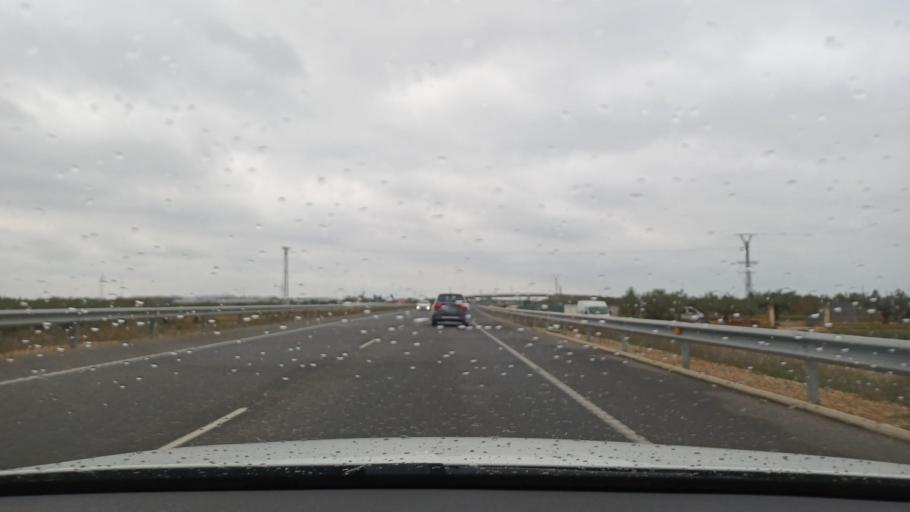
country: ES
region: Valencia
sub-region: Provincia de Castello
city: Benicarlo
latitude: 40.4189
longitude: 0.3876
